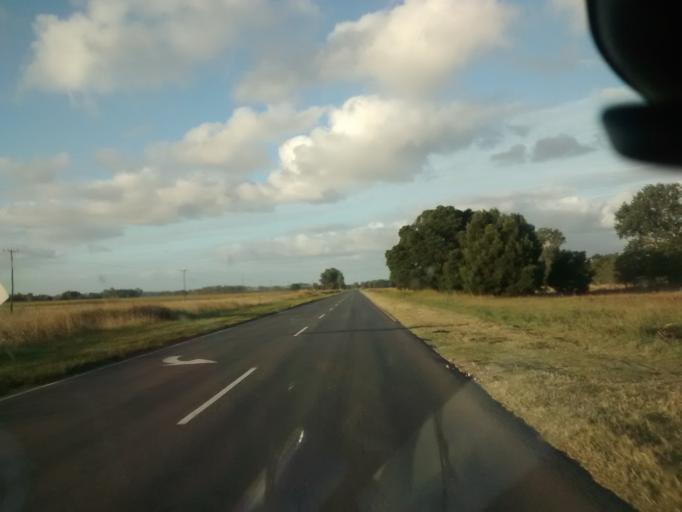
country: AR
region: Buenos Aires
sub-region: Partido de General Belgrano
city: General Belgrano
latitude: -35.7934
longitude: -58.5488
